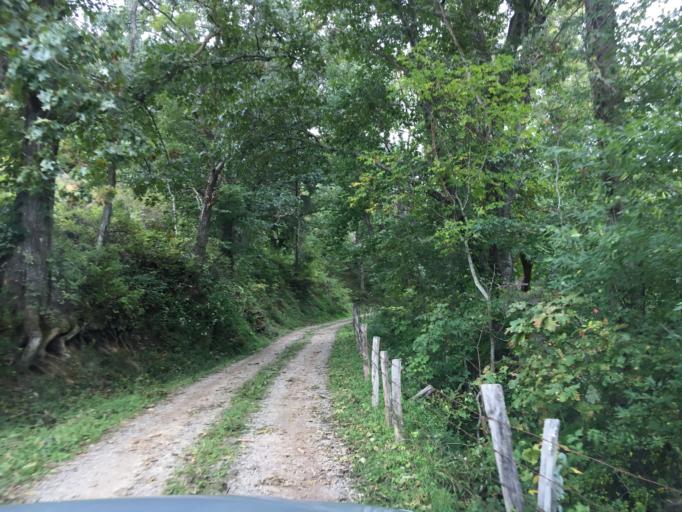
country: US
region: North Carolina
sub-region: Haywood County
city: Clyde
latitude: 35.5579
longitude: -82.9132
